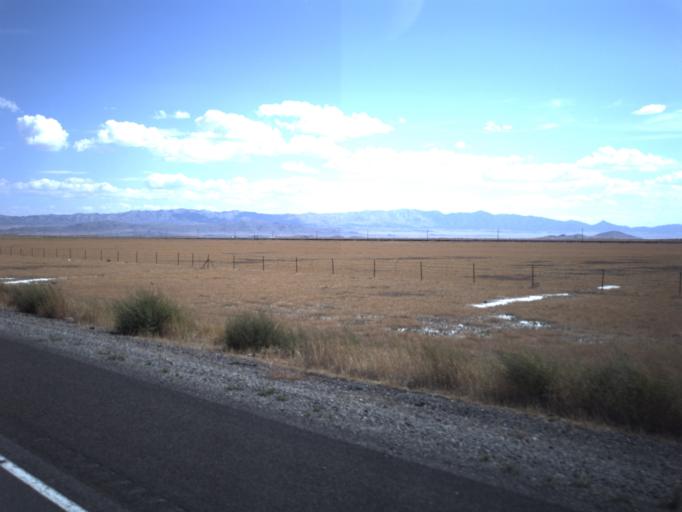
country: US
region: Utah
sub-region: Tooele County
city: Grantsville
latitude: 40.7262
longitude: -113.2343
